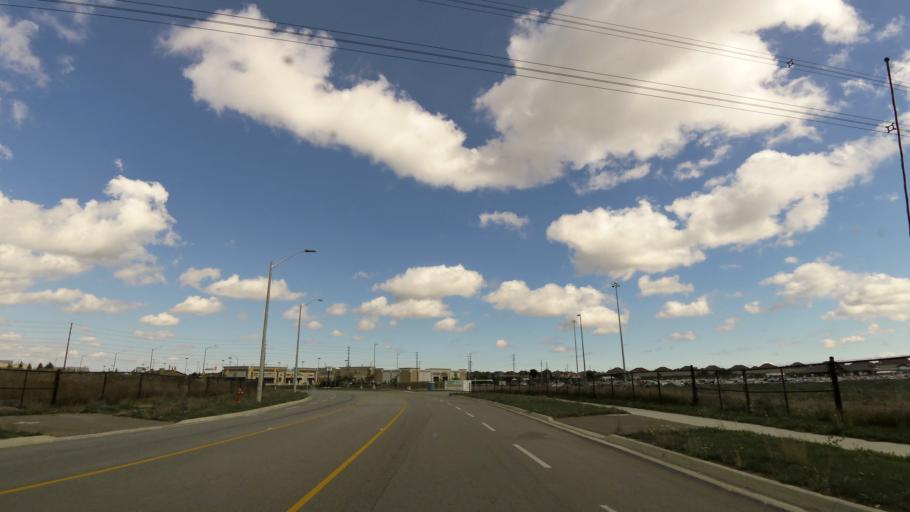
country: CA
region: Ontario
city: Brampton
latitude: 43.5925
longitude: -79.7910
